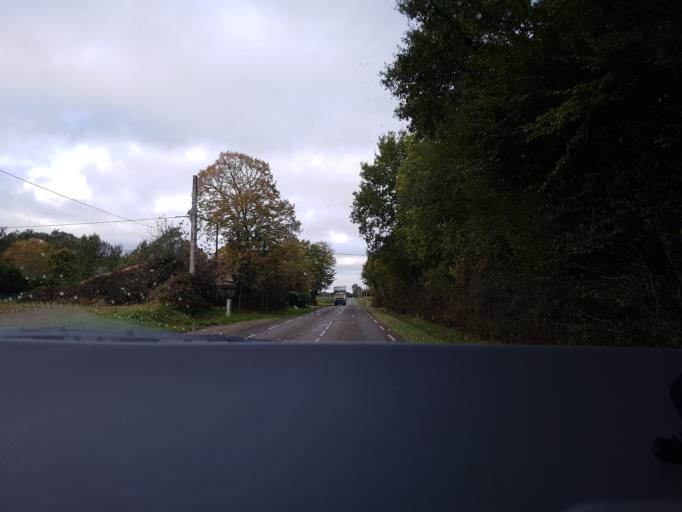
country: FR
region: Midi-Pyrenees
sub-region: Departement du Gers
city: Cazaubon
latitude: 43.9354
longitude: -0.1221
